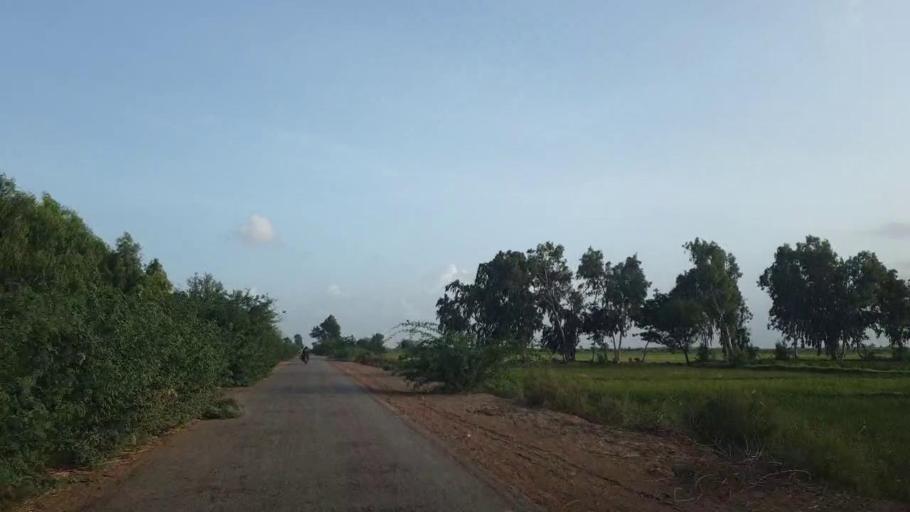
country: PK
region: Sindh
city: Kadhan
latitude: 24.6141
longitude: 69.1158
